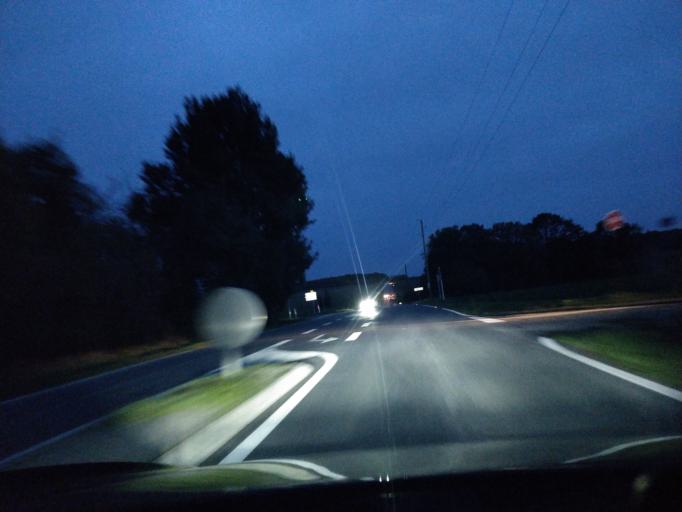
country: FR
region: Ile-de-France
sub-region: Departement de l'Essonne
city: Limours
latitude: 48.6299
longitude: 2.0665
